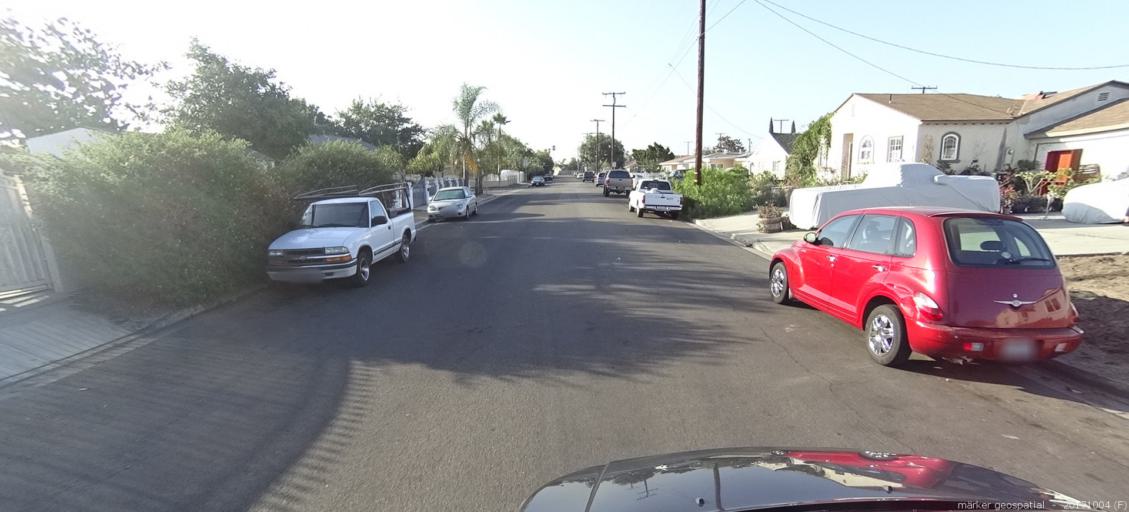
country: US
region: California
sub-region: Orange County
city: Garden Grove
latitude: 33.7725
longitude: -117.9156
